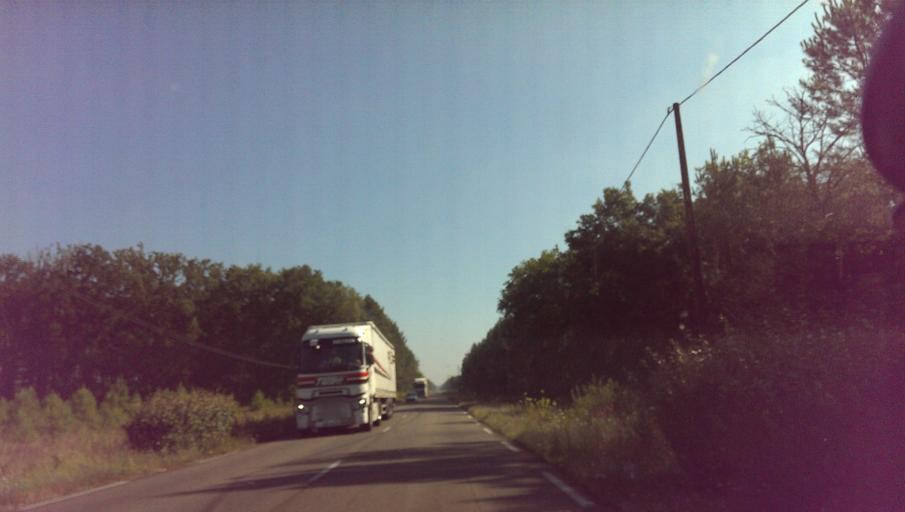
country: FR
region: Aquitaine
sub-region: Departement des Landes
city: Gabarret
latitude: 44.1066
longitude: -0.0106
